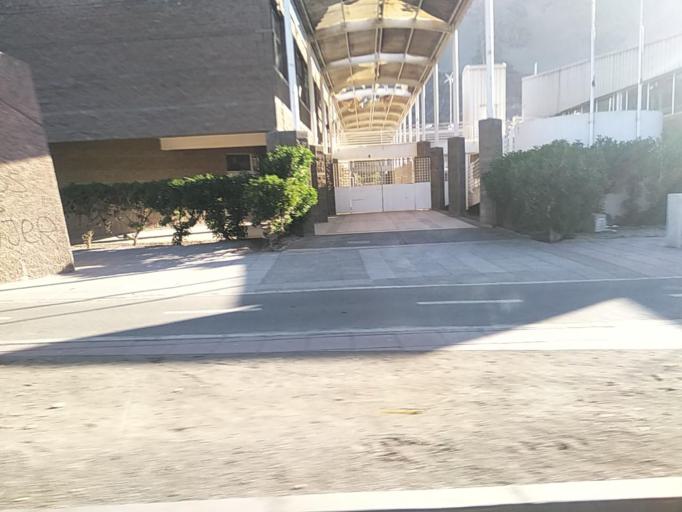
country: CL
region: Atacama
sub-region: Provincia de Copiapo
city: Copiapo
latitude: -27.3599
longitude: -70.3507
